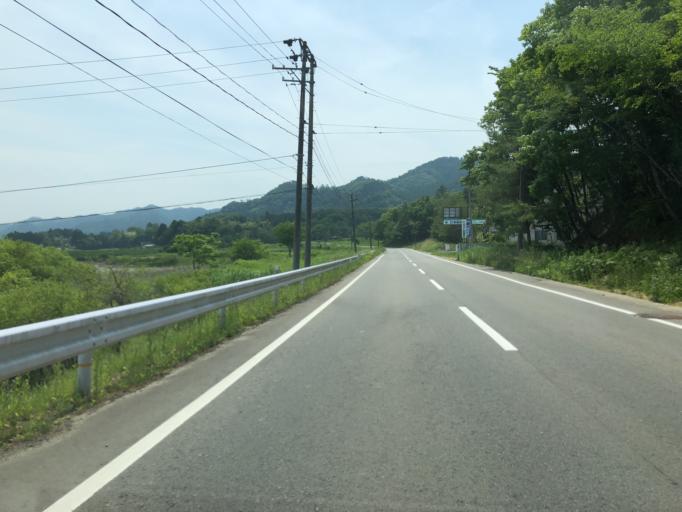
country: JP
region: Fukushima
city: Namie
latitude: 37.5255
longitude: 140.9337
